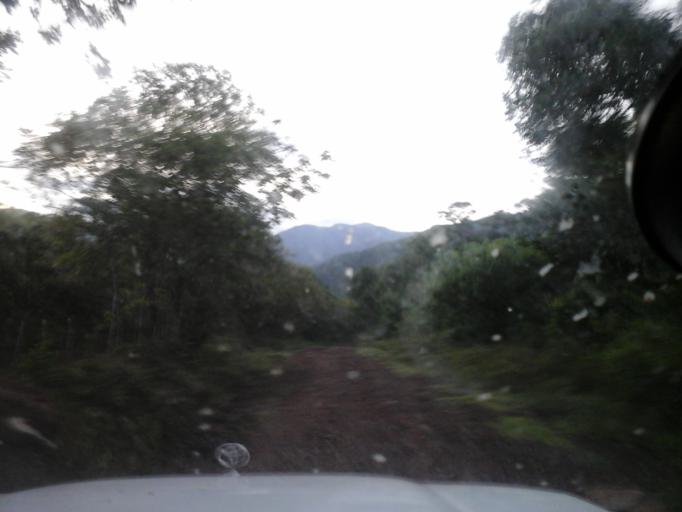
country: CO
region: Cesar
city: Agustin Codazzi
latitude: 10.1717
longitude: -73.1648
